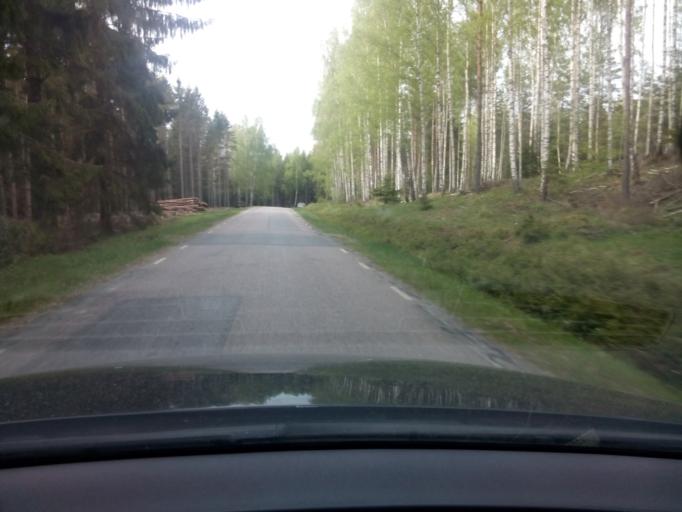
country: SE
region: Soedermanland
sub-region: Nykopings Kommun
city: Stigtomta
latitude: 58.9308
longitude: 16.8864
